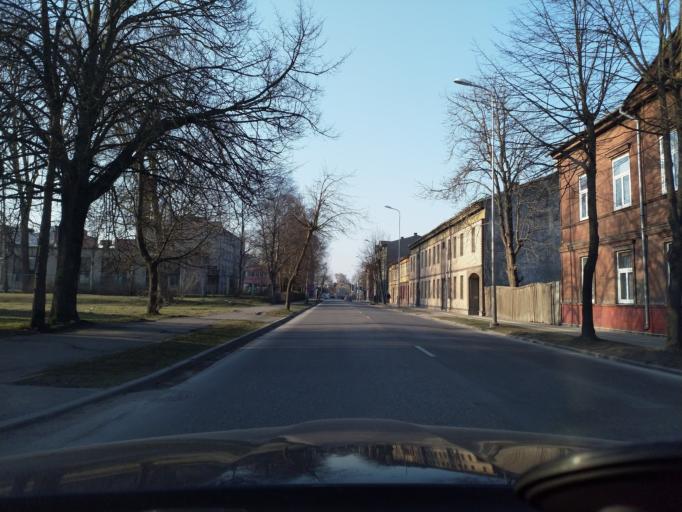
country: LV
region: Liepaja
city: Liepaja
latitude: 56.5040
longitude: 21.0193
